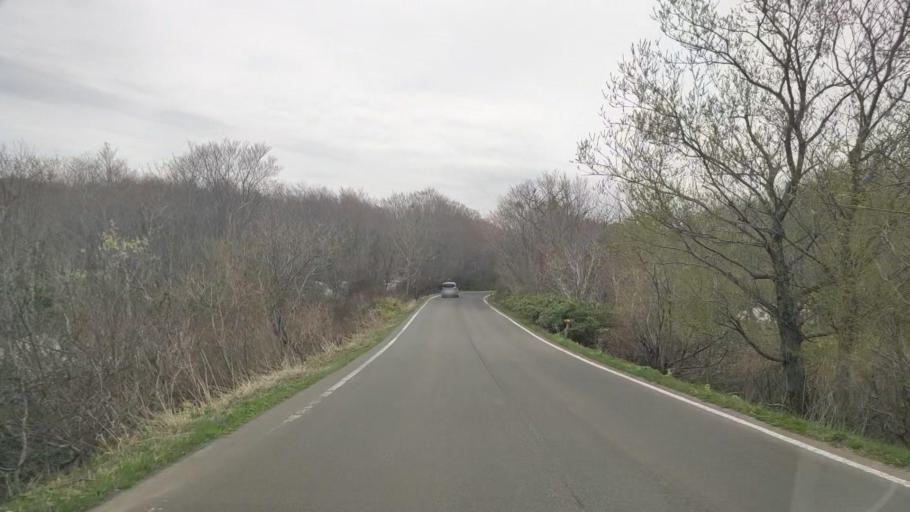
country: JP
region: Aomori
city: Aomori Shi
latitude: 40.6660
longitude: 140.9558
